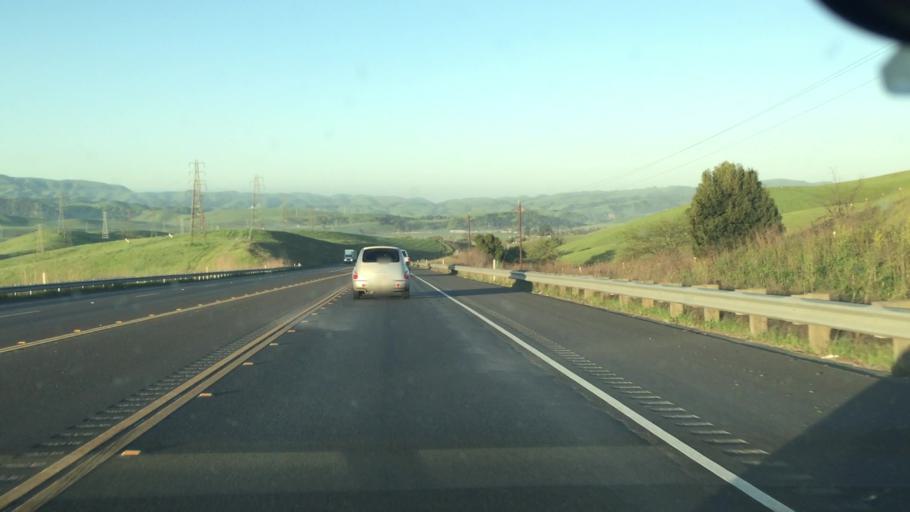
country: US
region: California
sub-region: Alameda County
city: Pleasanton
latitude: 37.6129
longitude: -121.8193
